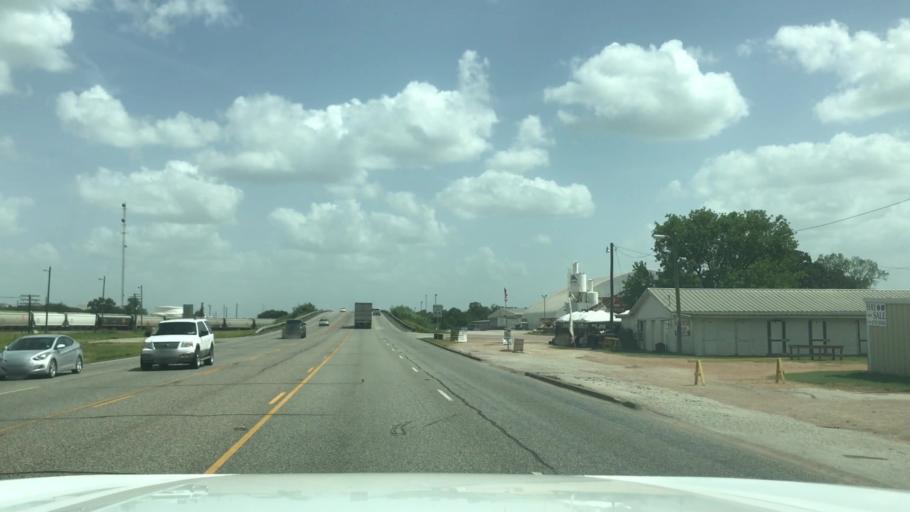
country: US
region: Texas
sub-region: Robertson County
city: Hearne
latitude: 30.8709
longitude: -96.5873
